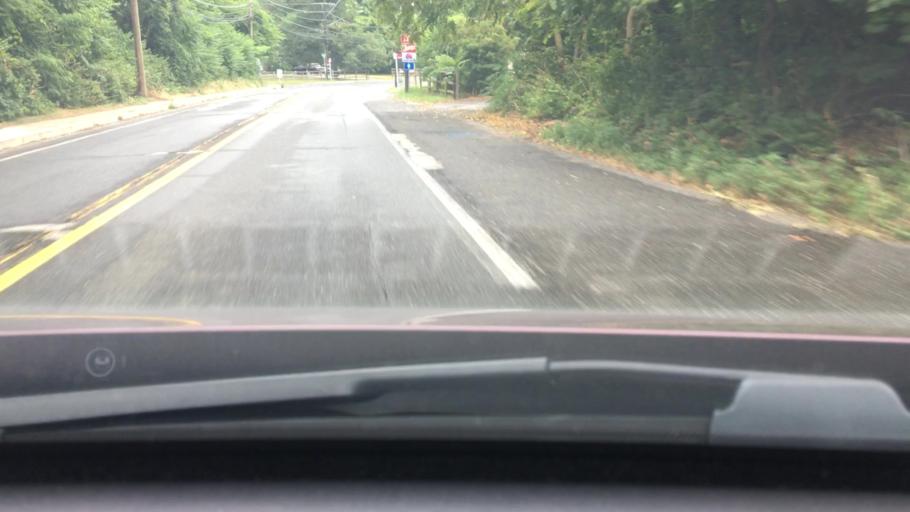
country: US
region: Maryland
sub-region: Prince George's County
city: Beltsville
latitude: 39.0446
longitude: -76.9131
